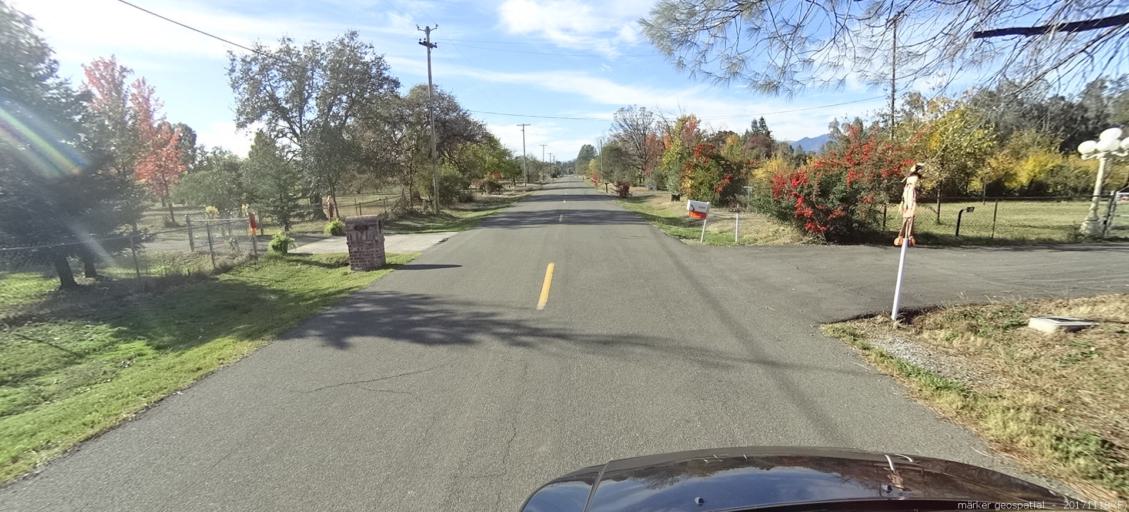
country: US
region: California
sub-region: Shasta County
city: Anderson
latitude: 40.4690
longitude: -122.4158
